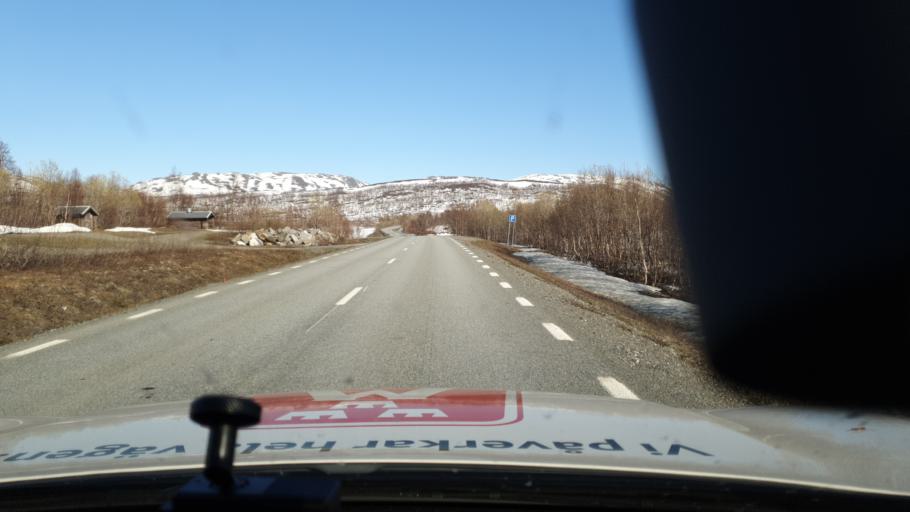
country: NO
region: Nordland
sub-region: Rana
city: Mo i Rana
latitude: 66.1214
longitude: 14.7915
